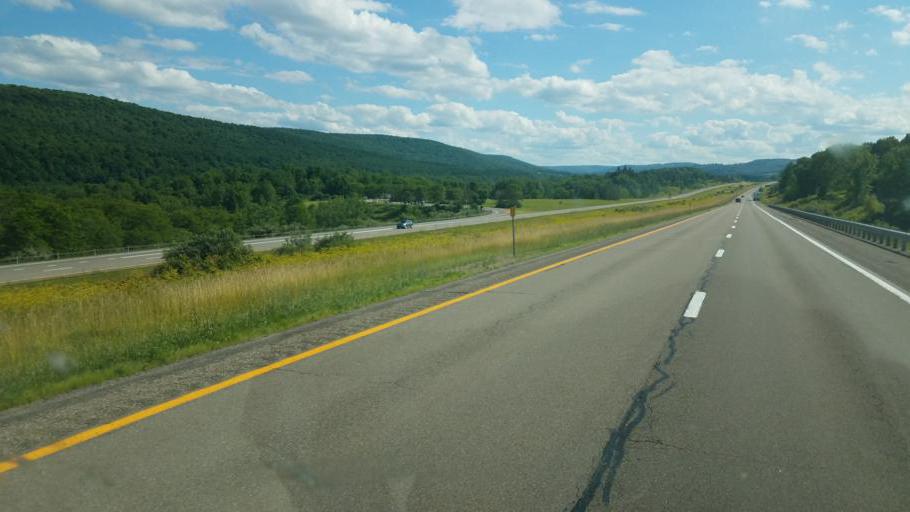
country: US
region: New York
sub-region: Steuben County
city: Hornell
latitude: 42.3451
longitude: -77.7249
